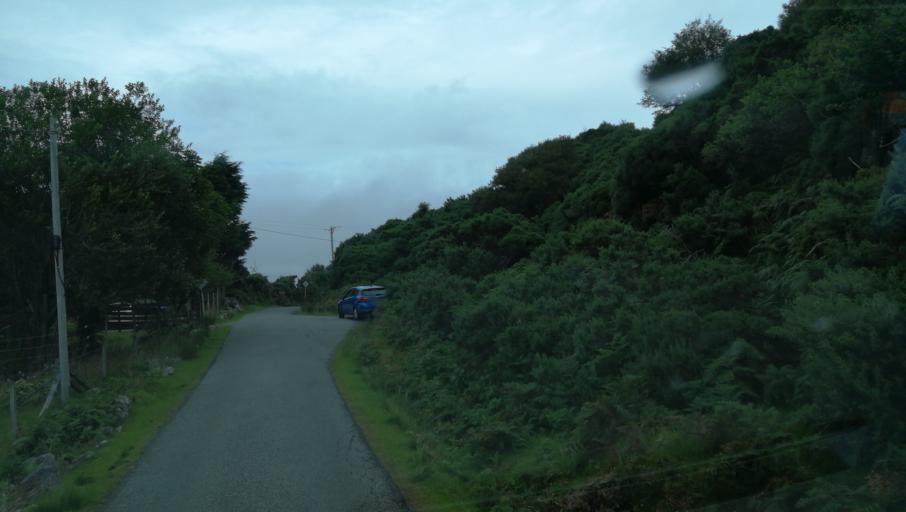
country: GB
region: Scotland
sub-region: Highland
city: Ullapool
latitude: 58.1356
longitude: -5.2623
